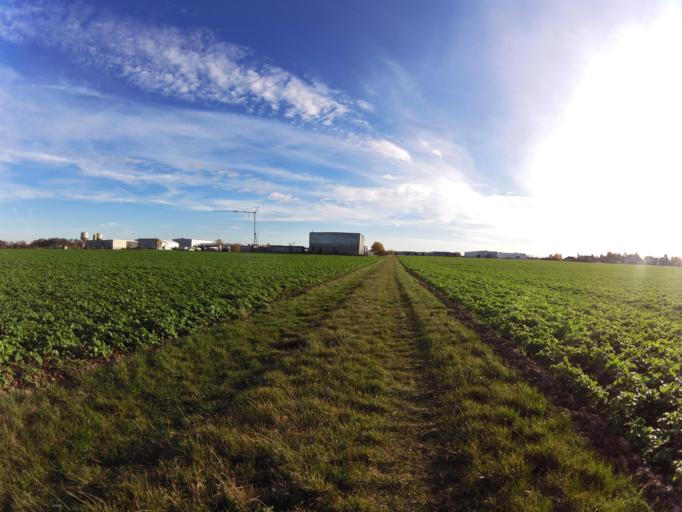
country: DE
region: Bavaria
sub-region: Regierungsbezirk Unterfranken
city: Giebelstadt
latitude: 49.6575
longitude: 9.9557
